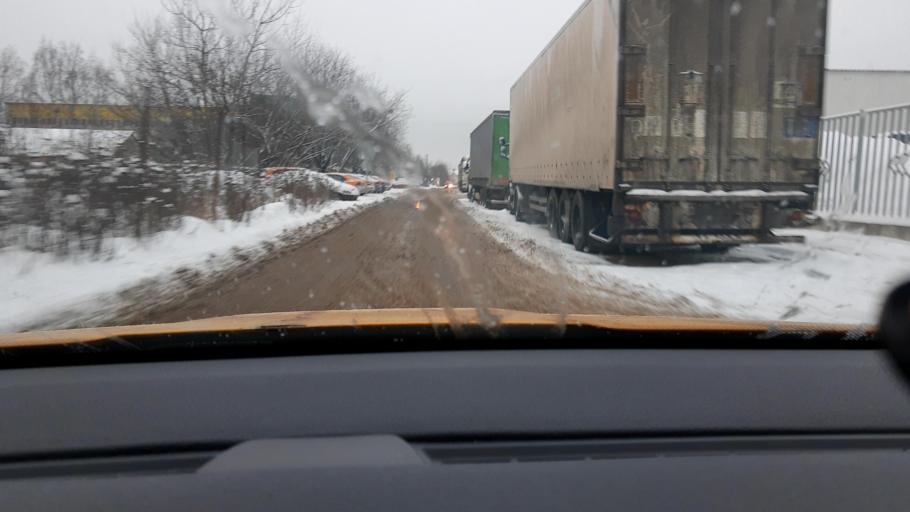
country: RU
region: Moscow
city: Businovo
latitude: 55.9134
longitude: 37.5008
